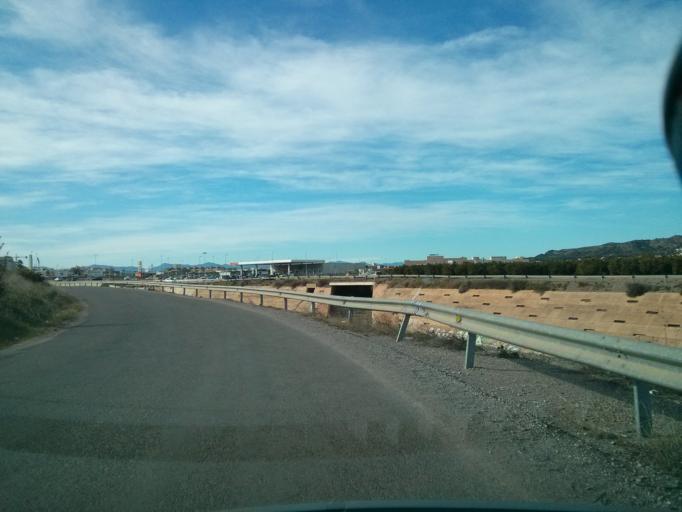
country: ES
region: Valencia
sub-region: Provincia de Castello
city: Castello de la Plana
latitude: 40.0032
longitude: -0.0291
